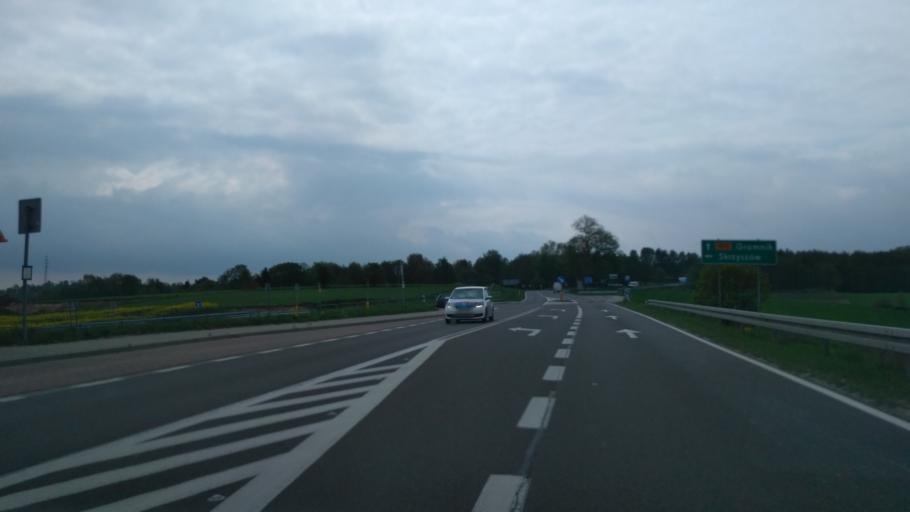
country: PL
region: Lesser Poland Voivodeship
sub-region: Powiat tarnowski
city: Tarnowiec
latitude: 49.9456
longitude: 21.0151
